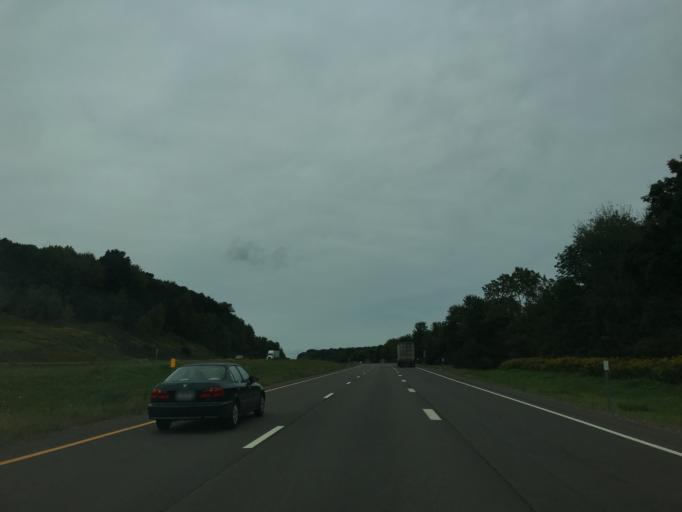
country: US
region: New York
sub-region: Broome County
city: Chenango Bridge
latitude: 42.1801
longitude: -75.7384
